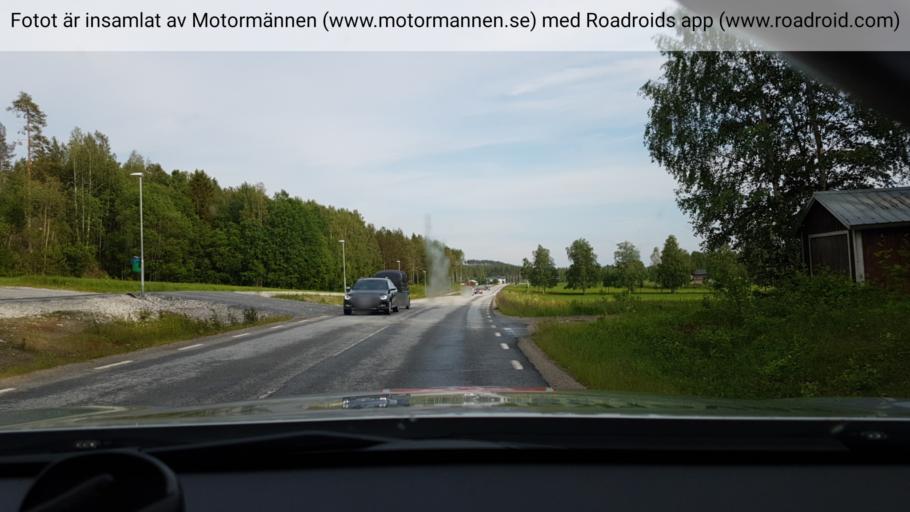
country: SE
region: Vaesterbotten
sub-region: Bjurholms Kommun
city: Bjurholm
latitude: 64.2392
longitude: 19.3377
